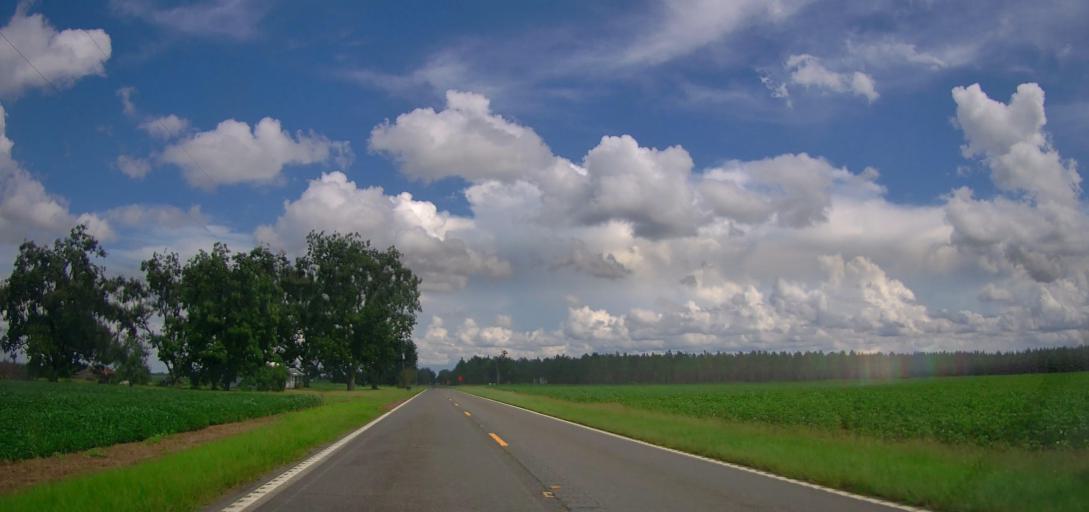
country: US
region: Georgia
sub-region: Taylor County
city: Reynolds
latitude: 32.4402
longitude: -84.1357
